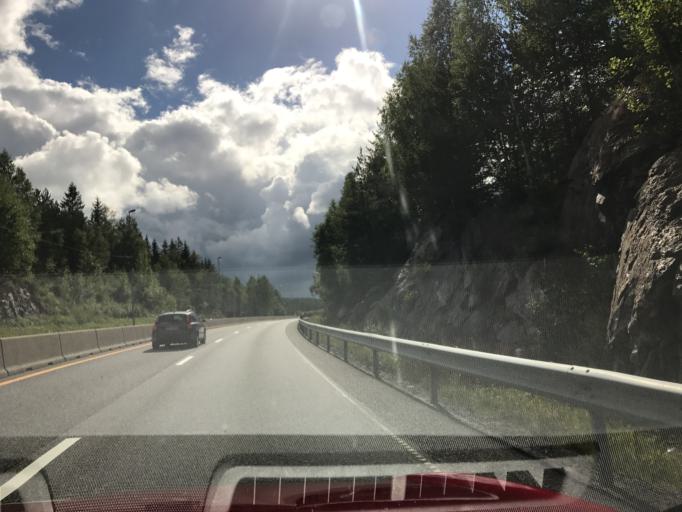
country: NO
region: Aust-Agder
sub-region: Gjerstad
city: Gjerstad
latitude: 58.8286
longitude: 9.0829
